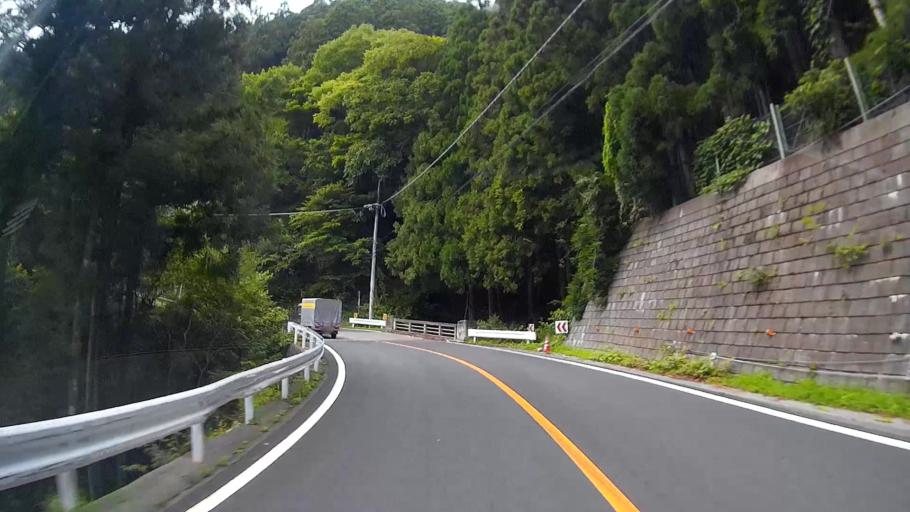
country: JP
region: Saitama
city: Chichibu
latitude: 35.9304
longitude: 138.8347
